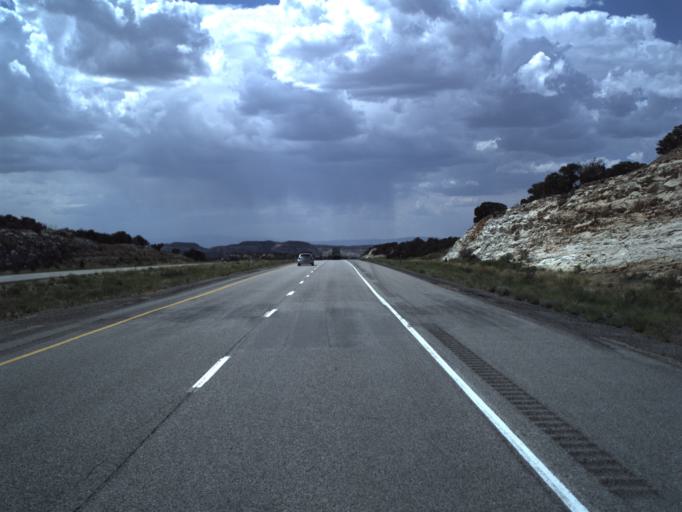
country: US
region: Utah
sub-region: Emery County
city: Ferron
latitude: 38.8595
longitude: -110.8247
